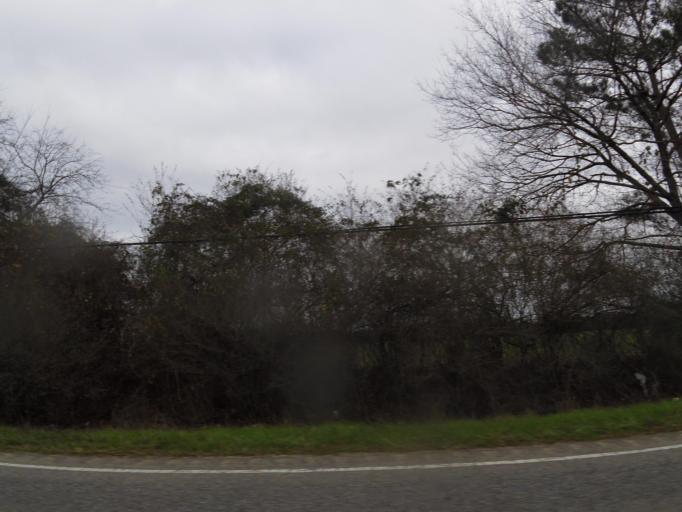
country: US
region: Alabama
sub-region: Barbour County
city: Eufaula
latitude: 31.9251
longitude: -85.1553
